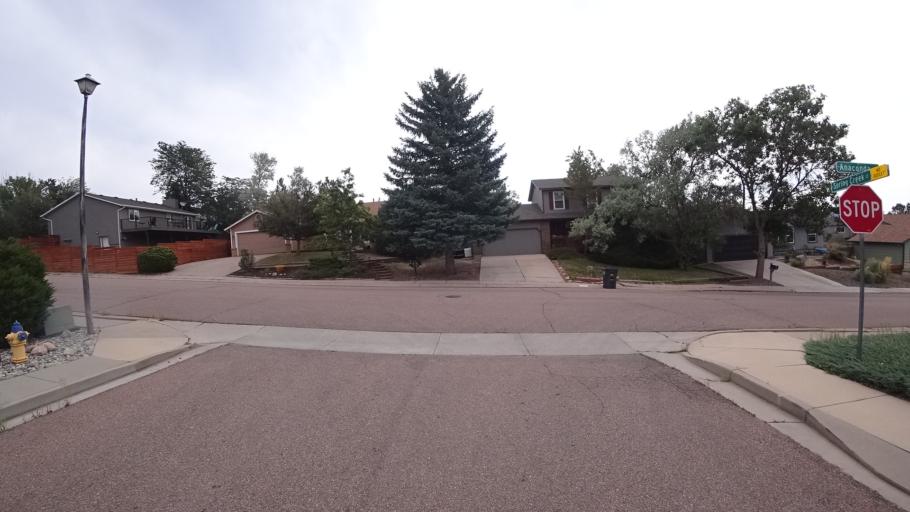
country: US
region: Colorado
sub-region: El Paso County
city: Air Force Academy
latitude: 38.9236
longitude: -104.8364
